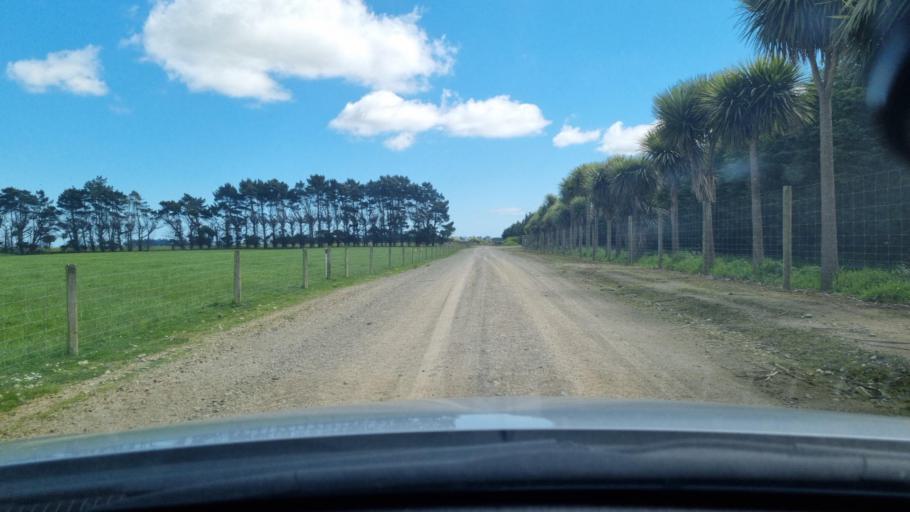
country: NZ
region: Southland
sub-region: Invercargill City
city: Invercargill
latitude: -46.3509
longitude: 168.3010
